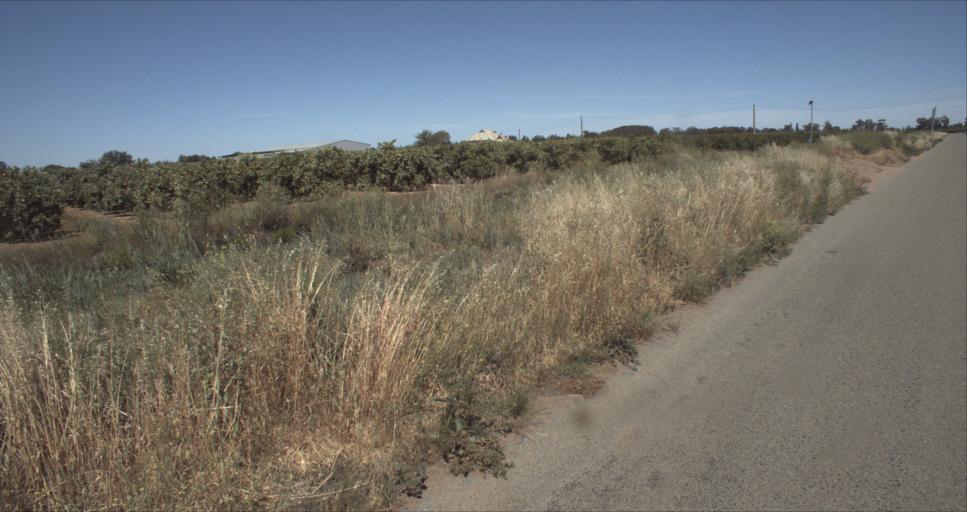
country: AU
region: New South Wales
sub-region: Leeton
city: Leeton
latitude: -34.5350
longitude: 146.3526
